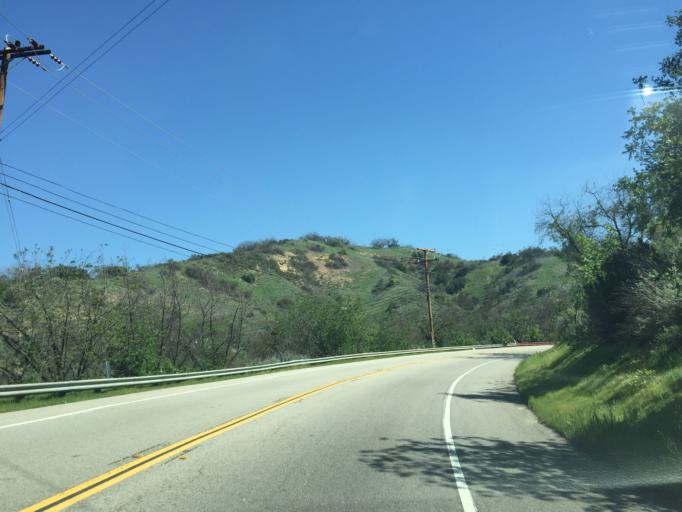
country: US
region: California
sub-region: Los Angeles County
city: Topanga
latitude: 34.1267
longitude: -118.6003
